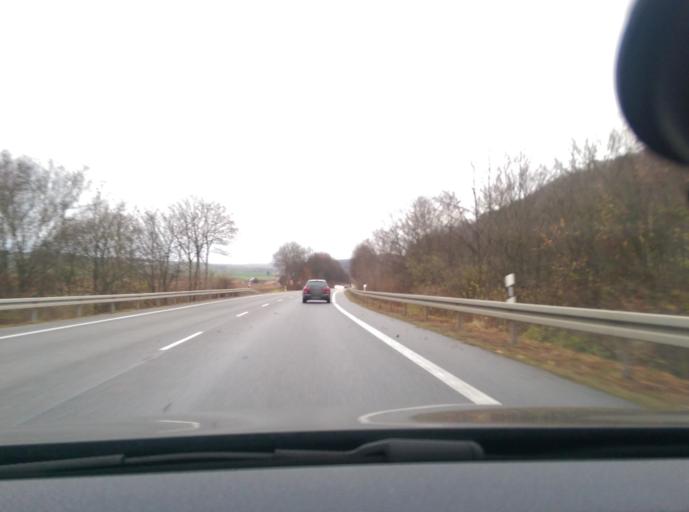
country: DE
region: Lower Saxony
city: Gemeinde Friedland
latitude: 51.4012
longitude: 9.9042
